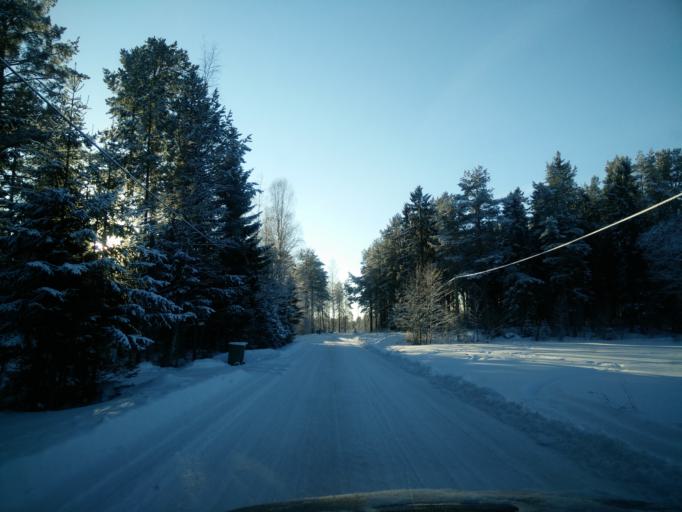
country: SE
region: Vaesternorrland
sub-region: Sundsvalls Kommun
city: Njurundabommen
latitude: 62.2315
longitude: 17.5054
